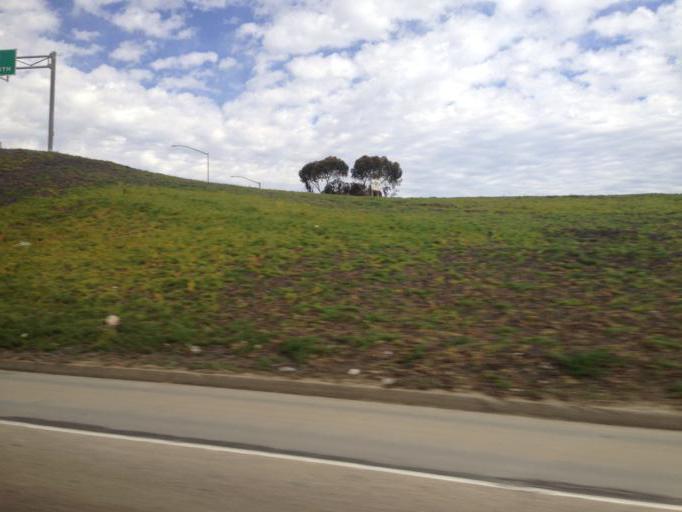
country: US
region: California
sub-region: San Diego County
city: Bonita
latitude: 32.6052
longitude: -117.0361
